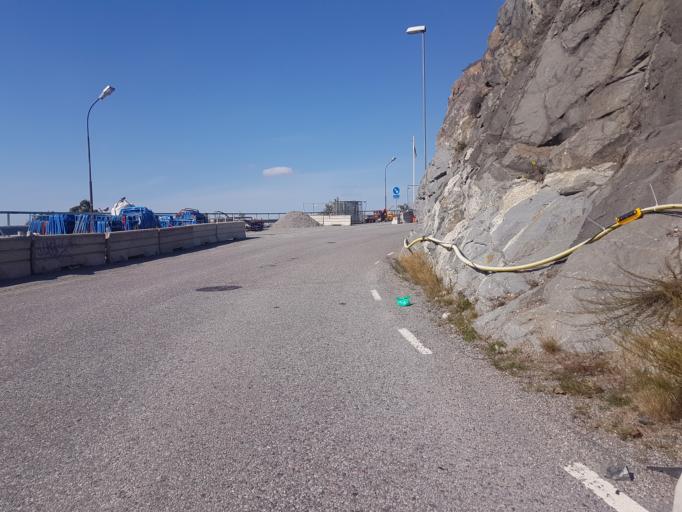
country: SE
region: Stockholm
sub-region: Nacka Kommun
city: Nacka
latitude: 59.3159
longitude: 18.1323
